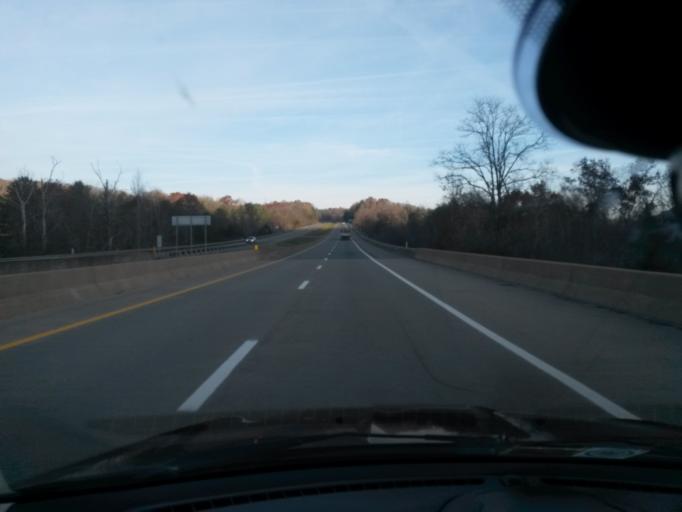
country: US
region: West Virginia
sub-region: Greenbrier County
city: Lewisburg
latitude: 37.7921
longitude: -80.3848
